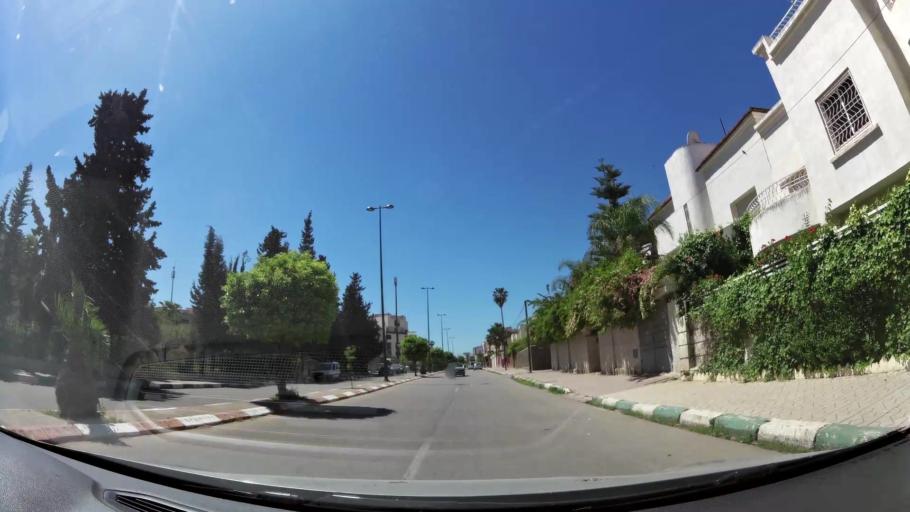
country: MA
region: Meknes-Tafilalet
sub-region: Meknes
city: Meknes
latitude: 33.9041
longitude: -5.5324
